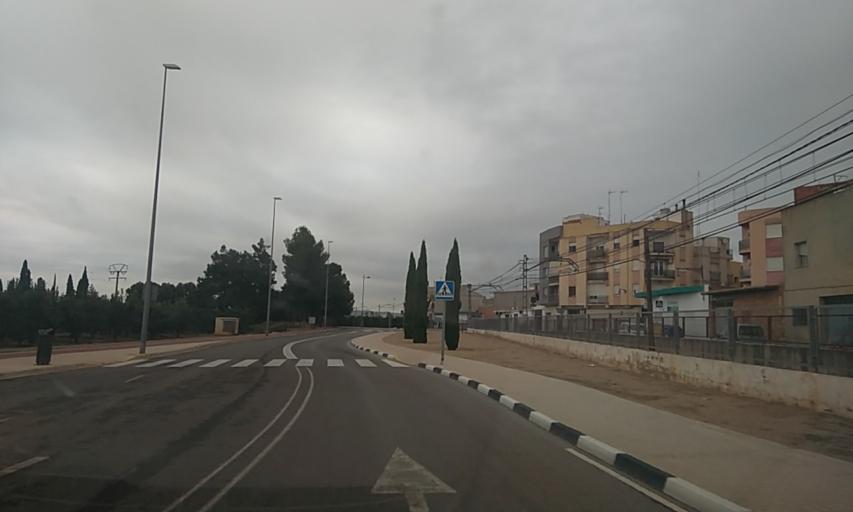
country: ES
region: Valencia
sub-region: Provincia de Valencia
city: L'Alcudia
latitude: 39.1984
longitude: -0.5098
